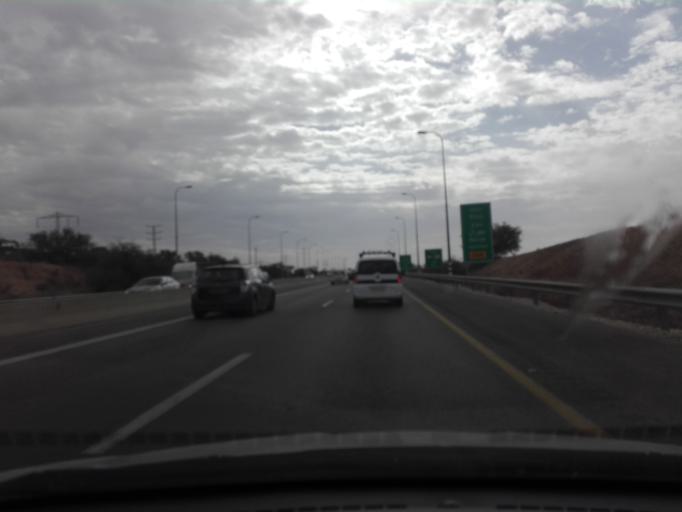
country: IL
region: Southern District
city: Lehavim
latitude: 31.3184
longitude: 34.7873
